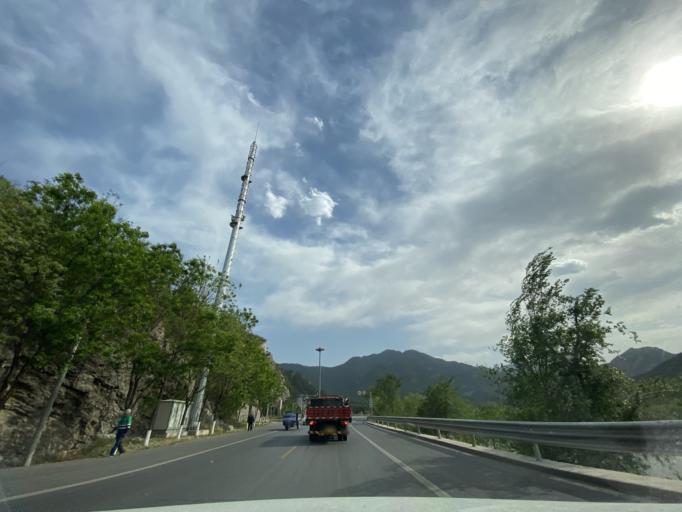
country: CN
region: Beijing
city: Miaofengshan
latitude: 39.9818
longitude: 116.0606
